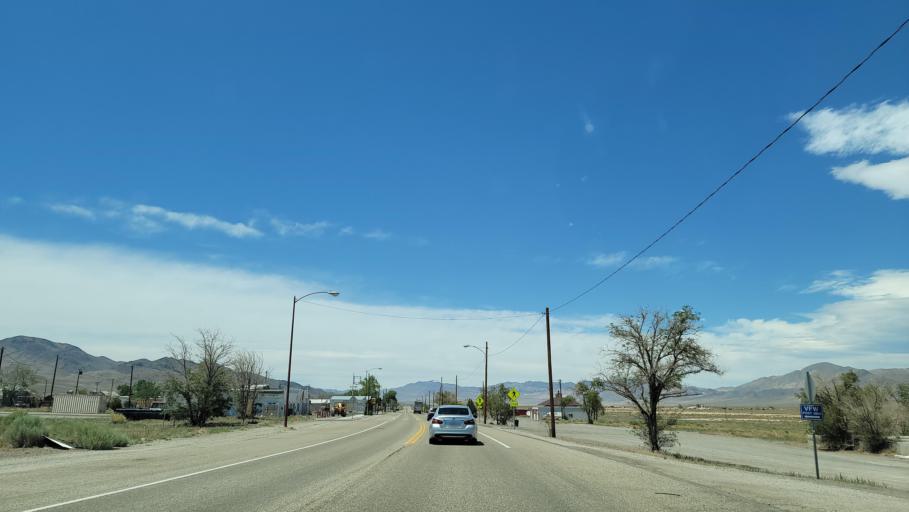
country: US
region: Nevada
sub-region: Mineral County
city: Hawthorne
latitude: 38.3889
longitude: -118.1077
